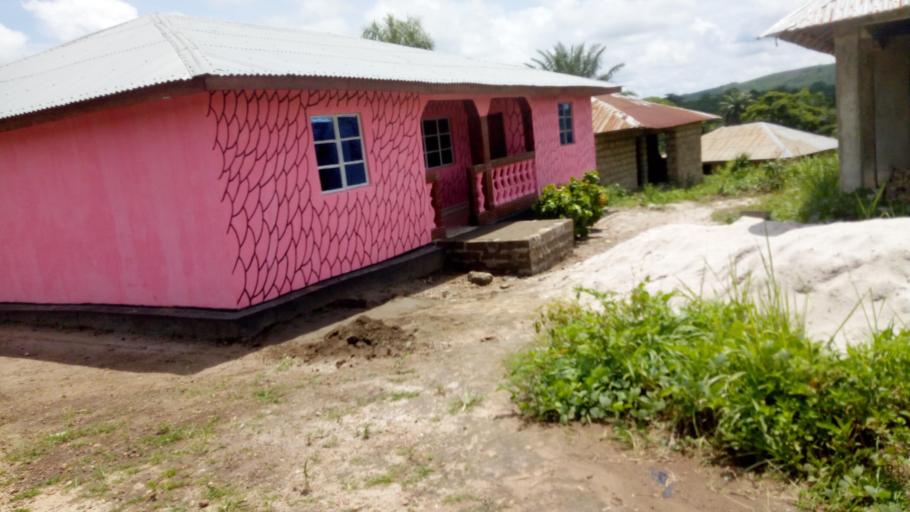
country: SL
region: Northern Province
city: Magburaka
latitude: 8.7207
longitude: -11.9601
